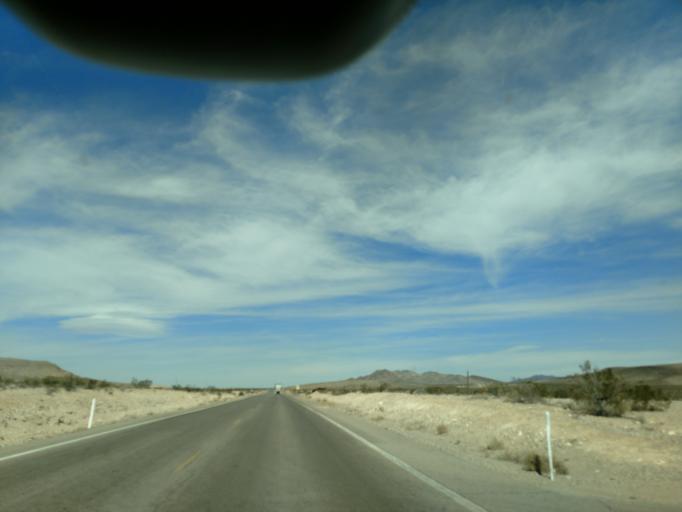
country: US
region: Nevada
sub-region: Clark County
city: Enterprise
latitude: 35.8549
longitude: -115.2560
